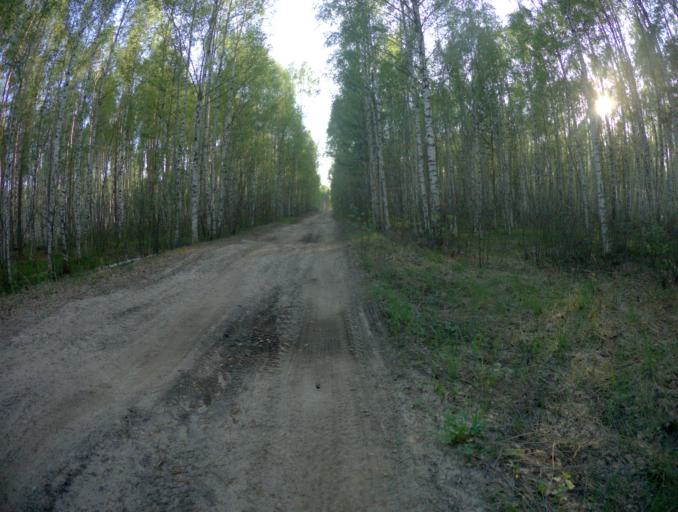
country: RU
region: Vladimir
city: Vyazniki
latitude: 56.3746
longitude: 42.1700
